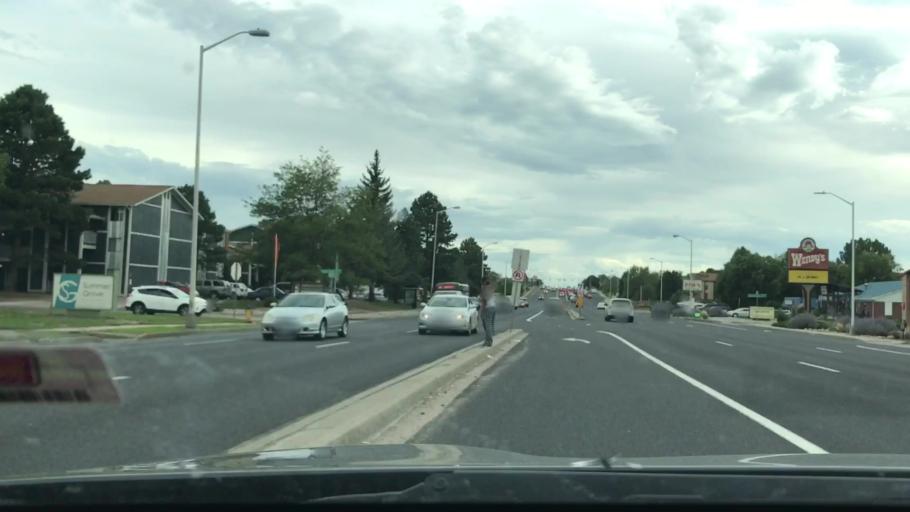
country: US
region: Colorado
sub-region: El Paso County
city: Cimarron Hills
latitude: 38.8866
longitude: -104.7570
